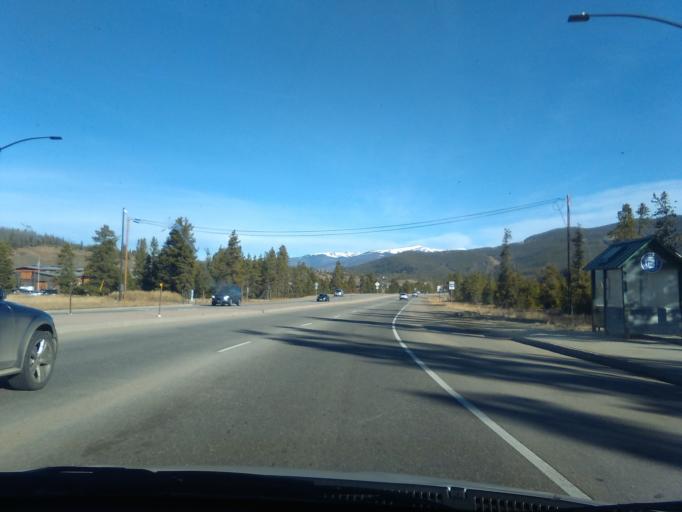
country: US
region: Colorado
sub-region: Summit County
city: Breckenridge
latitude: 39.5262
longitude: -106.0451
